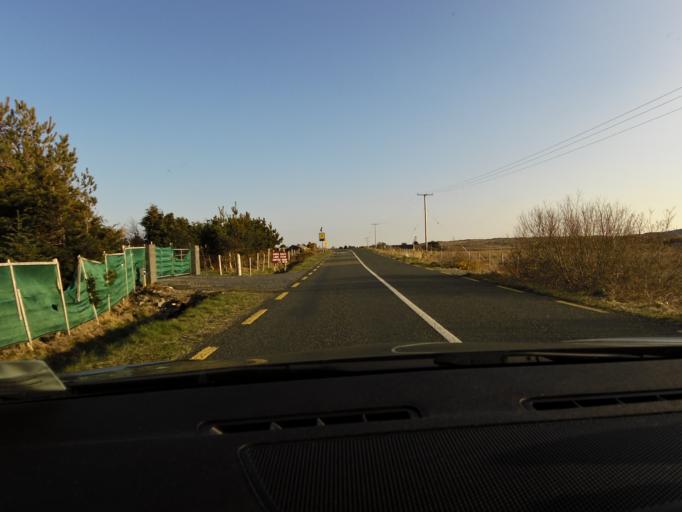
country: IE
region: Connaught
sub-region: County Galway
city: Oughterard
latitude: 53.3800
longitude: -9.5492
